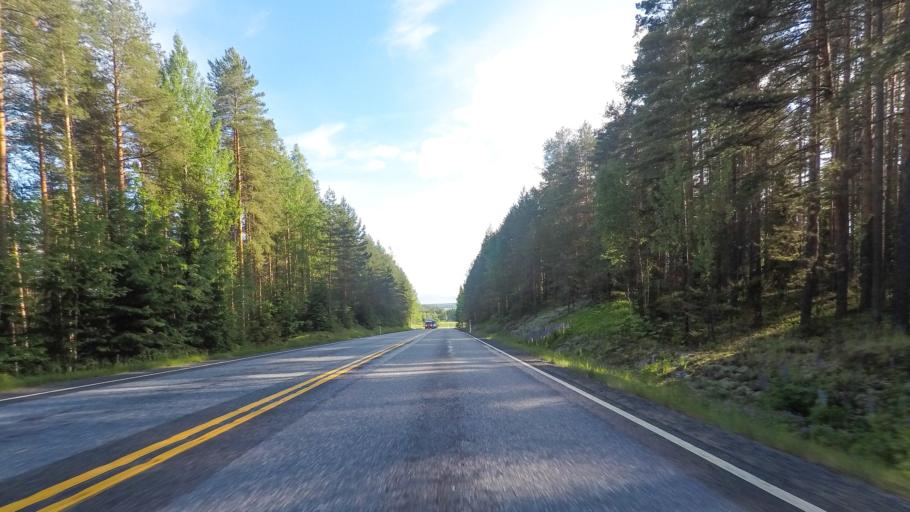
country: FI
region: Paijanne Tavastia
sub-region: Lahti
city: Hartola
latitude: 61.6627
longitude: 26.0311
